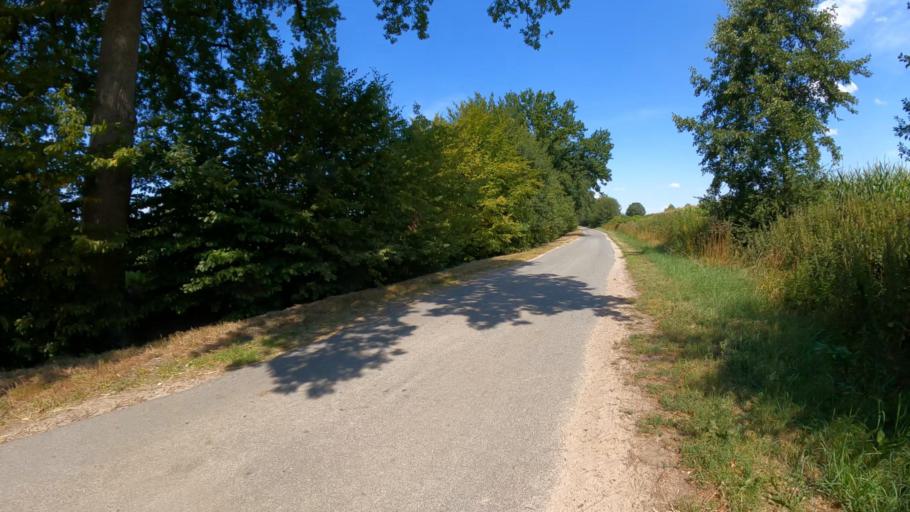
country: DE
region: Schleswig-Holstein
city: Borstel-Hohenraden
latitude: 53.7098
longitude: 9.8288
